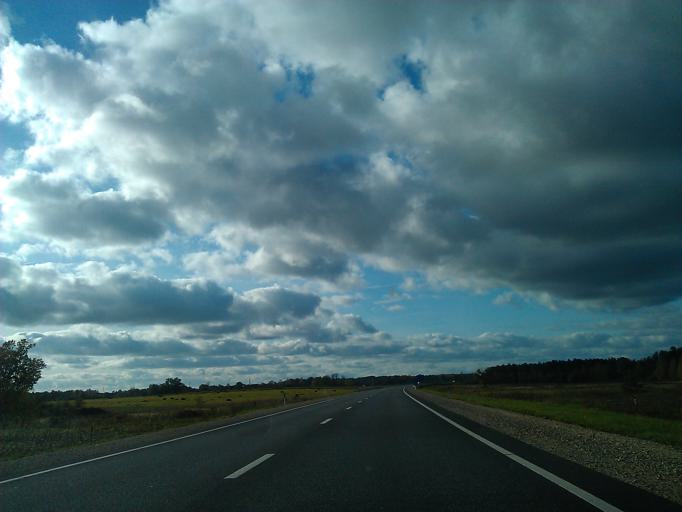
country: LV
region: Ogre
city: Jumprava
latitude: 56.7789
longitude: 25.0301
